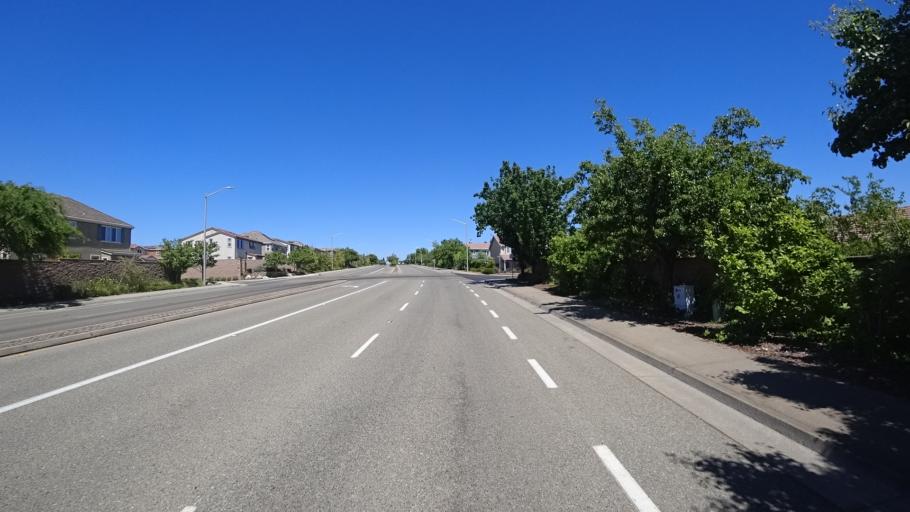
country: US
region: California
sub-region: Placer County
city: Rocklin
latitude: 38.8154
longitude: -121.2751
